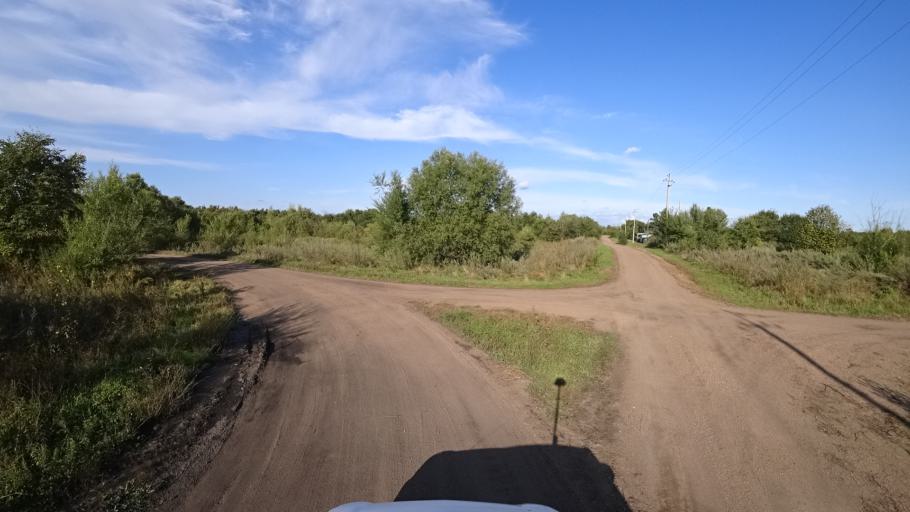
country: RU
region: Amur
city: Arkhara
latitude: 49.3505
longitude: 130.1056
